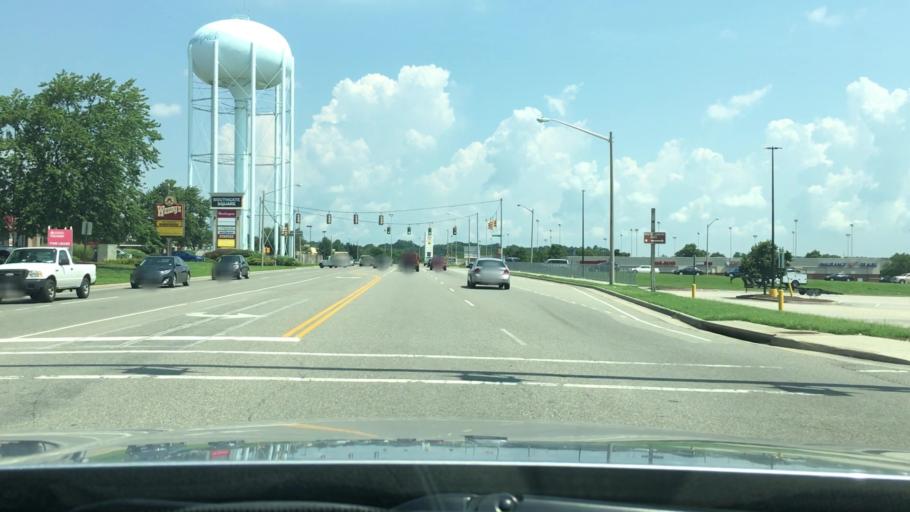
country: US
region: Virginia
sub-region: City of Petersburg
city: Petersburg
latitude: 37.2463
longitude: -77.3896
